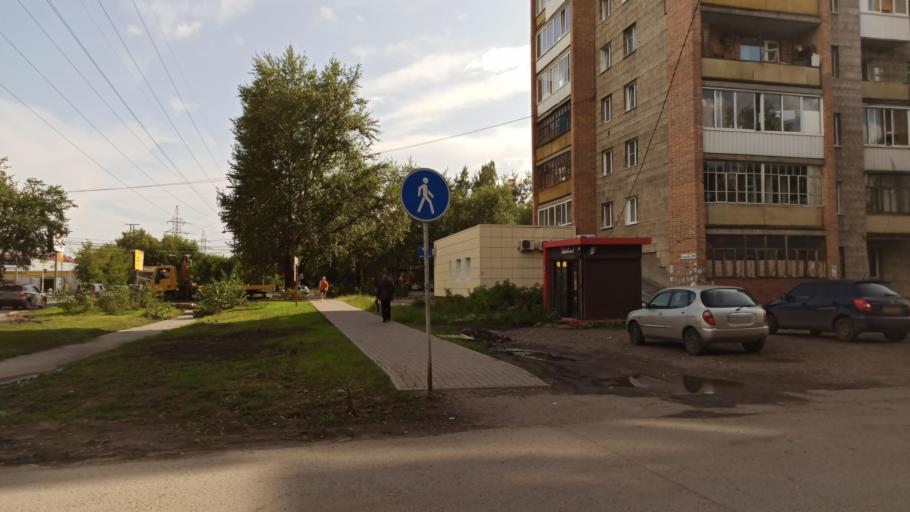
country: RU
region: Tomsk
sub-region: Tomskiy Rayon
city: Tomsk
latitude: 56.4770
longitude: 84.9997
